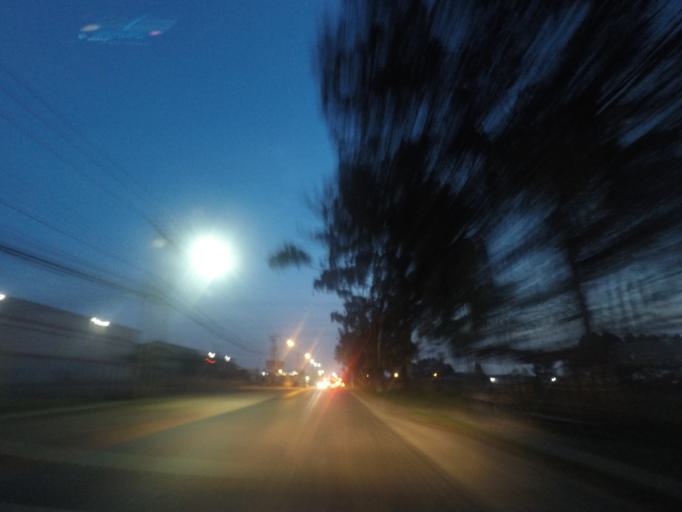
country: BR
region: Parana
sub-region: Pinhais
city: Pinhais
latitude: -25.4896
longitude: -49.1571
